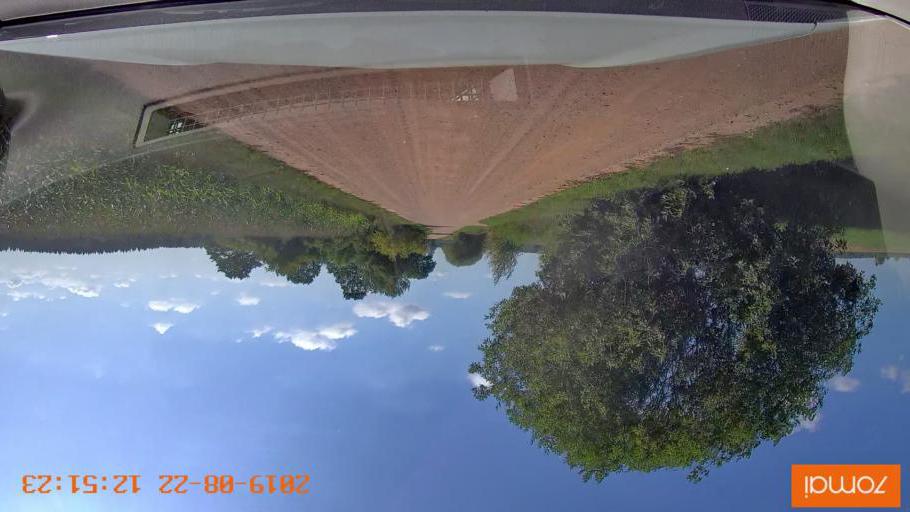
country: BY
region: Minsk
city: Prawdzinski
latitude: 53.4583
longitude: 27.6541
